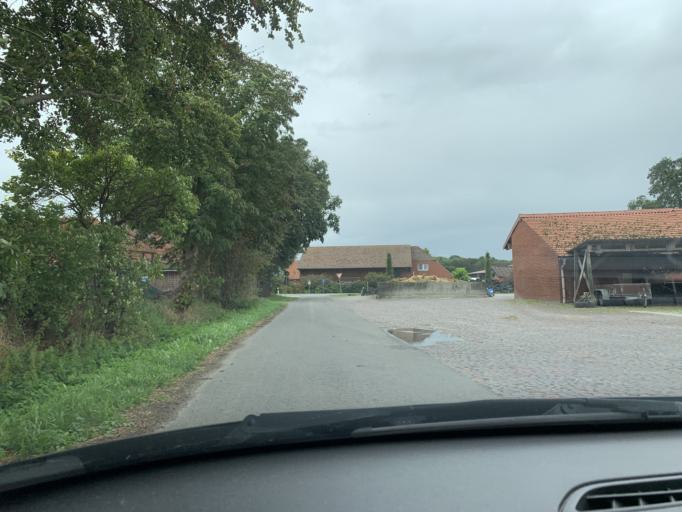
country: DE
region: Lower Saxony
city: Westerstede
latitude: 53.2438
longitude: 7.8856
